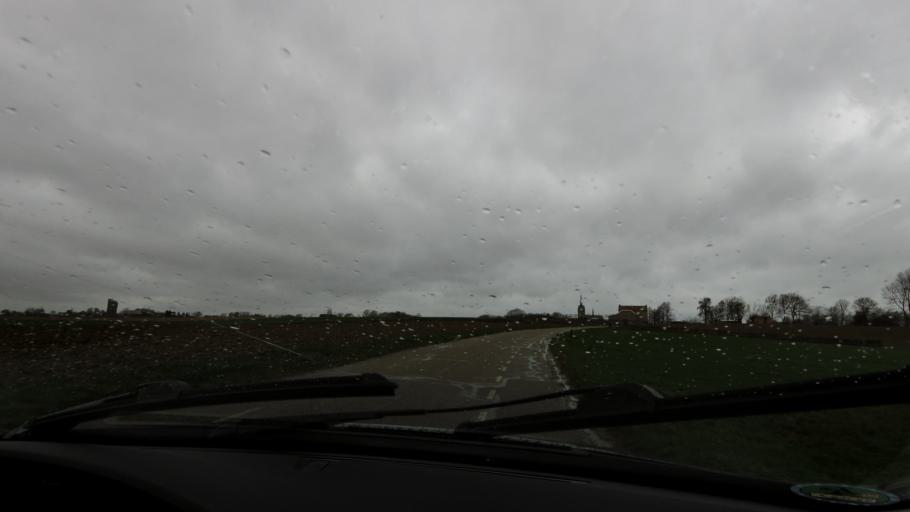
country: NL
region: Limburg
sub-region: Valkenburg aan de Geul
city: Broekhem
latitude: 50.9050
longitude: 5.8375
